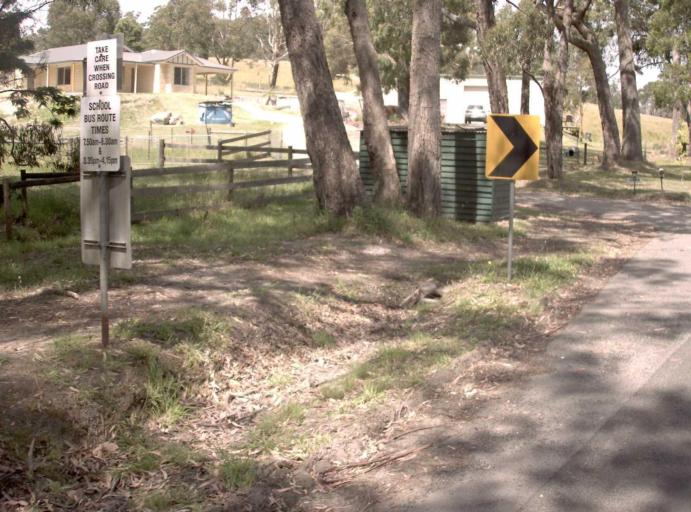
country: AU
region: Victoria
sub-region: Latrobe
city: Traralgon
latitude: -38.3057
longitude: 146.5437
